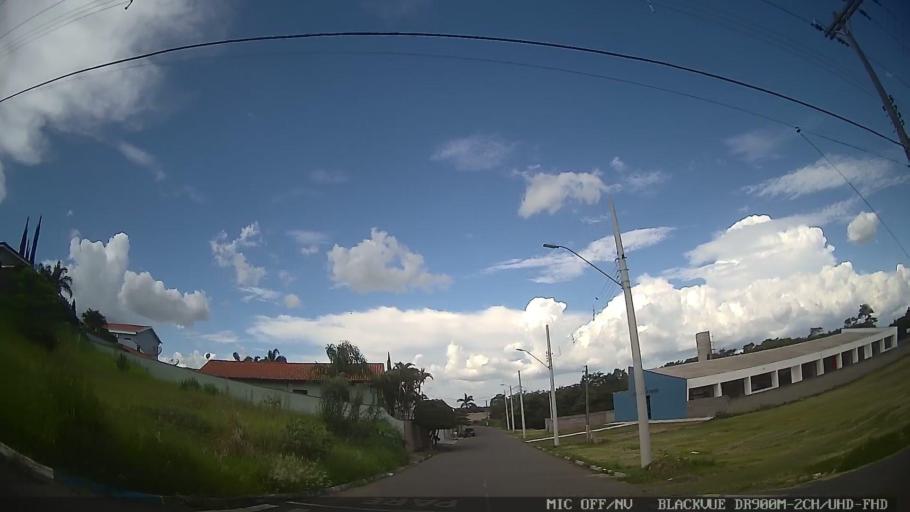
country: BR
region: Sao Paulo
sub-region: Conchas
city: Conchas
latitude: -23.0180
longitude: -48.0085
